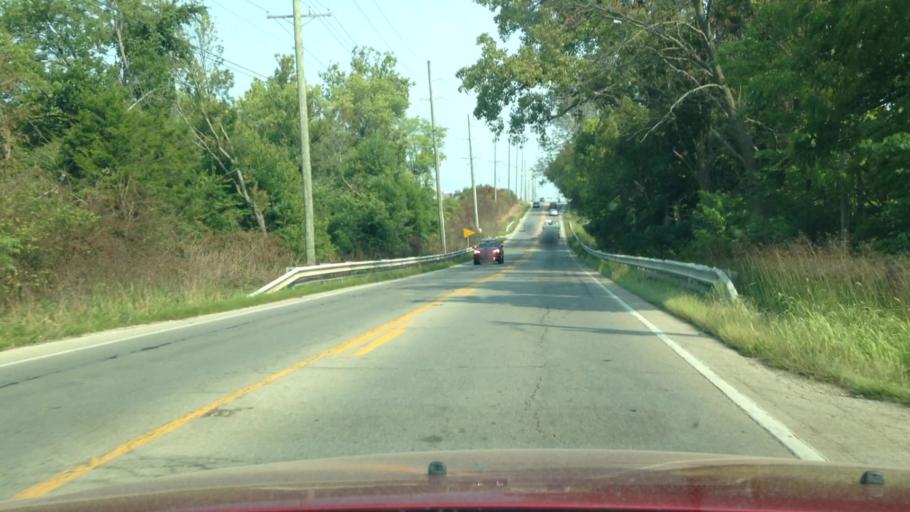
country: US
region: Indiana
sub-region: Johnson County
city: Waterloo
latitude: 39.5666
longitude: -86.1588
